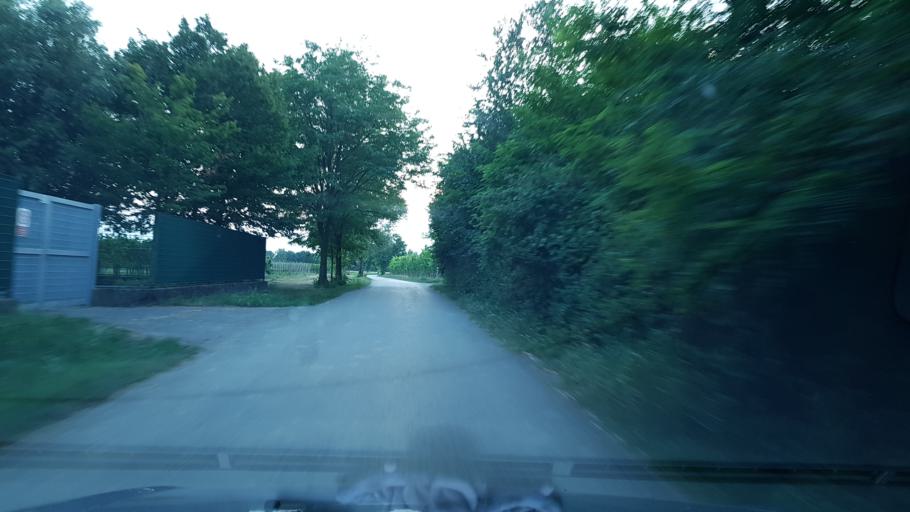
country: IT
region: Friuli Venezia Giulia
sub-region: Provincia di Gorizia
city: San Pier d'Isonzo
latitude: 45.8382
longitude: 13.4608
